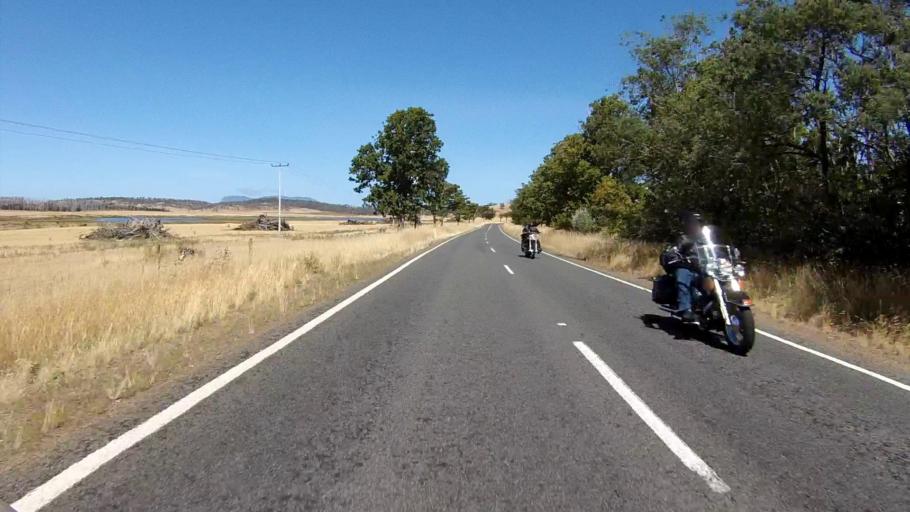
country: AU
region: Tasmania
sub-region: Sorell
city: Sorell
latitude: -42.4799
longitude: 147.9319
